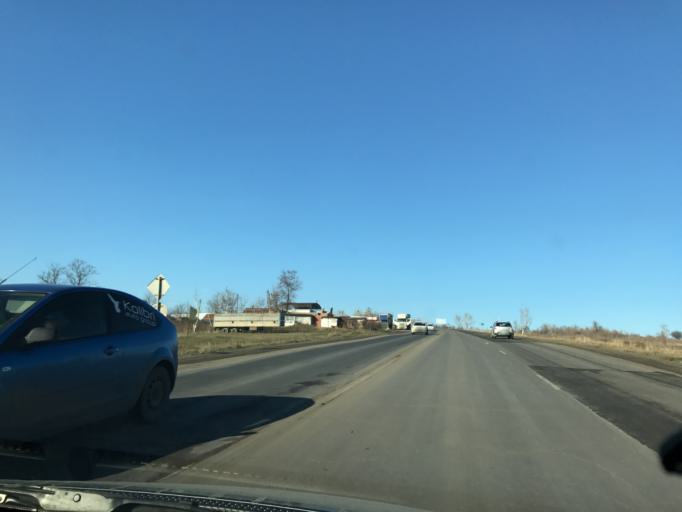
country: RU
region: Rostov
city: Kagal'nitskaya
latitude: 46.8865
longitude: 40.1427
